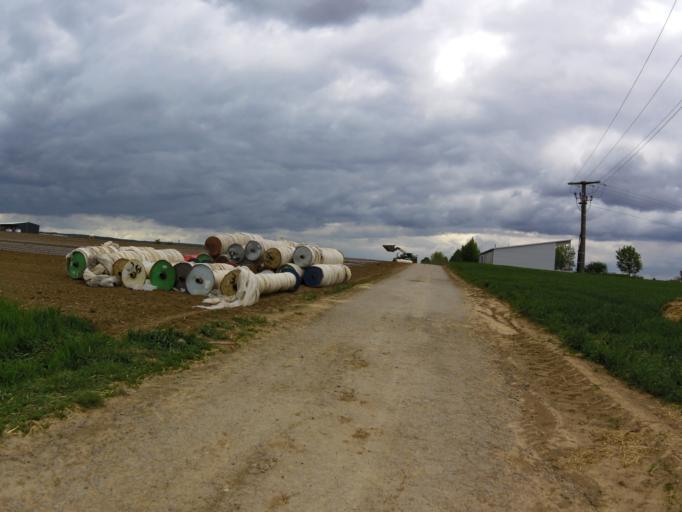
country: DE
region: Bavaria
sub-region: Regierungsbezirk Unterfranken
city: Unterpleichfeld
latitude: 49.8617
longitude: 10.0472
